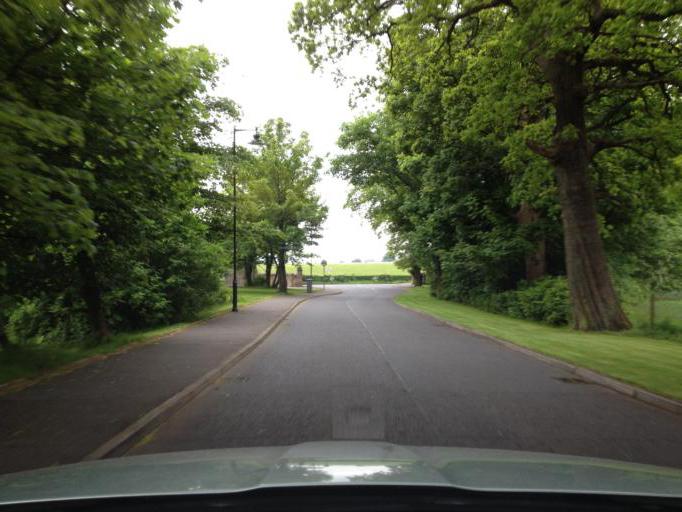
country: GB
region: Scotland
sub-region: Renfrewshire
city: Bishopton
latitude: 55.9171
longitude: -4.4890
